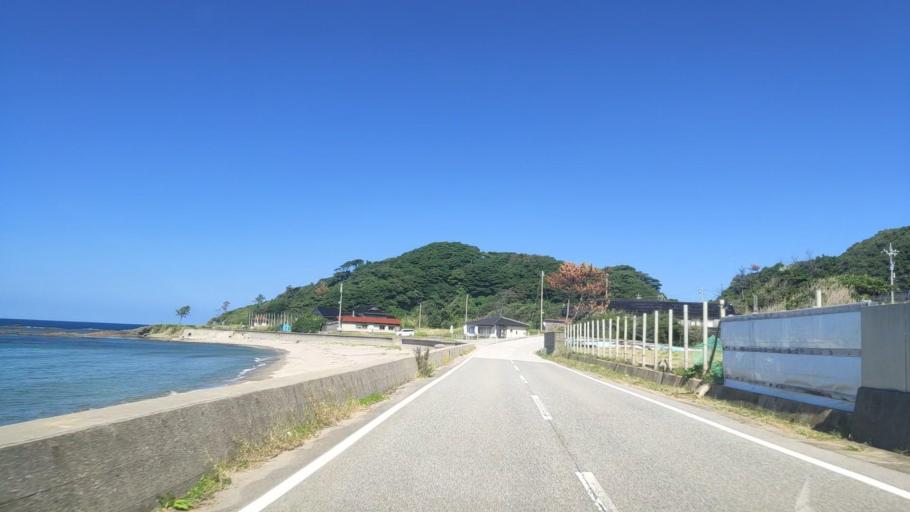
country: JP
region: Ishikawa
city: Nanao
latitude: 37.5113
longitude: 137.2194
